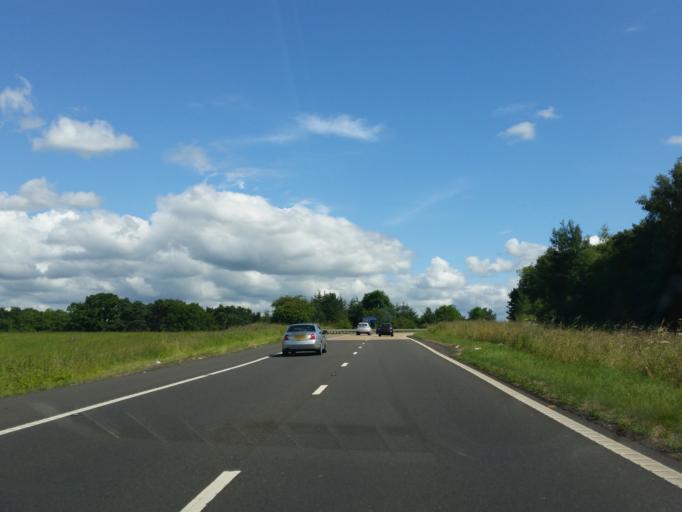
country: GB
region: Scotland
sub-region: South Lanarkshire
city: Larkhall
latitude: 55.7550
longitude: -3.9697
